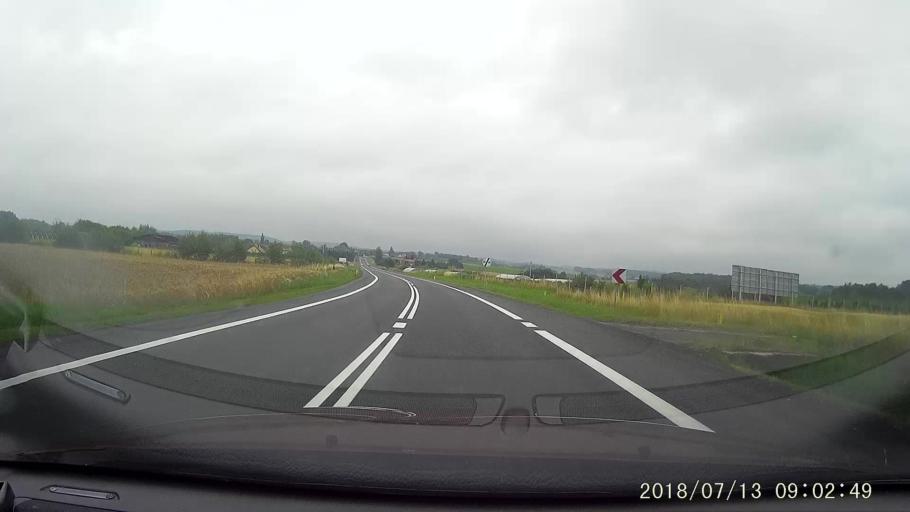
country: PL
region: Lower Silesian Voivodeship
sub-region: Powiat zgorzelecki
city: Lagow
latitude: 51.1524
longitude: 15.0815
